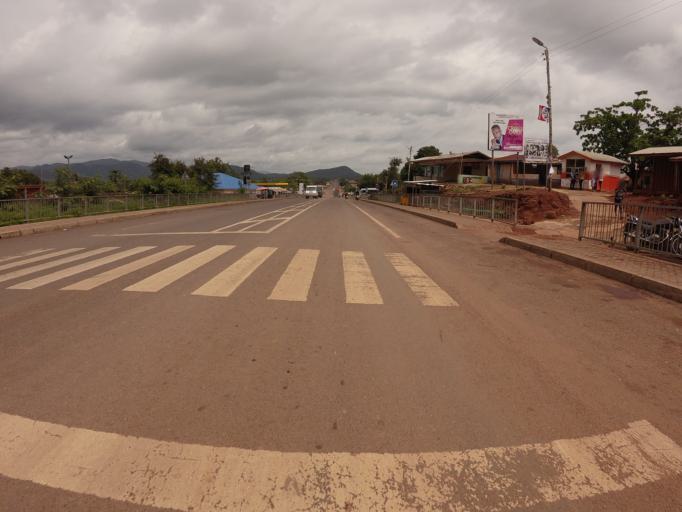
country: TG
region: Centrale
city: Sotouboua
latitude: 8.2585
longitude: 0.5222
